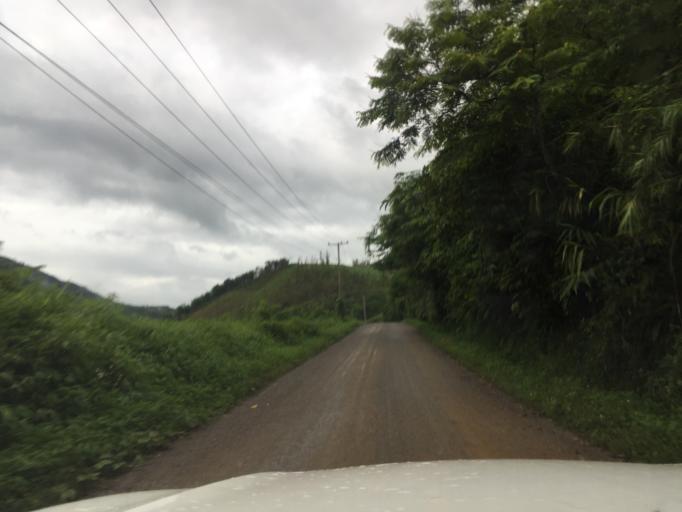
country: LA
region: Oudomxai
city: Muang La
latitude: 20.9722
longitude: 102.2224
